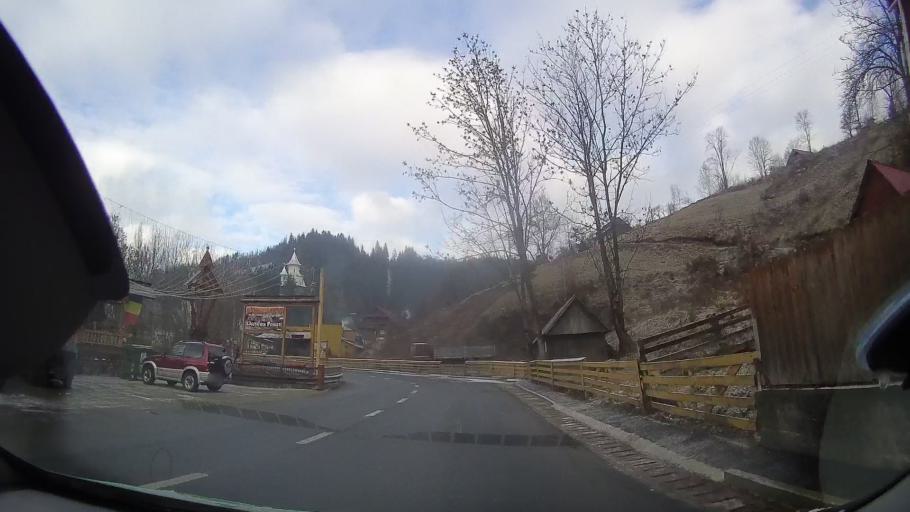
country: RO
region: Alba
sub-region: Comuna Horea
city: Horea
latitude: 46.4998
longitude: 22.9506
